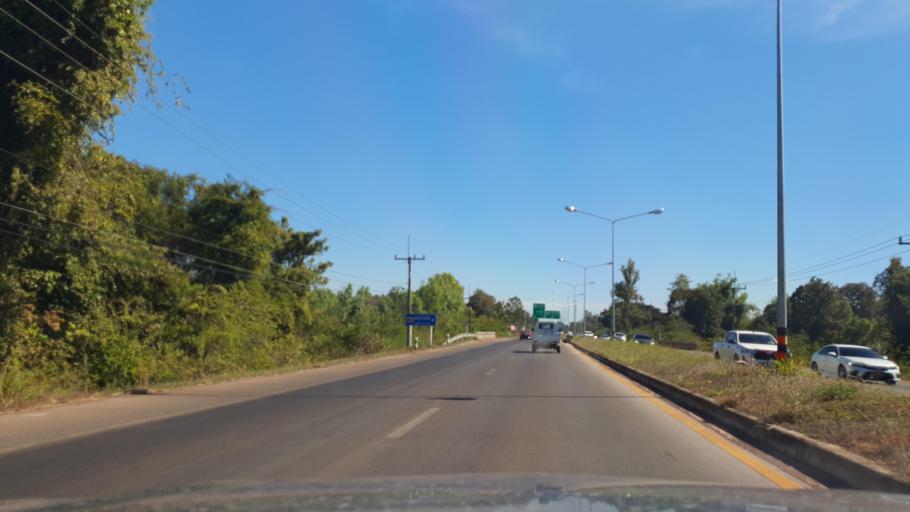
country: TH
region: Sakon Nakhon
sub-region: Amphoe Khok Si Suphan
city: Khok Si Suphan
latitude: 17.0719
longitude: 104.2114
